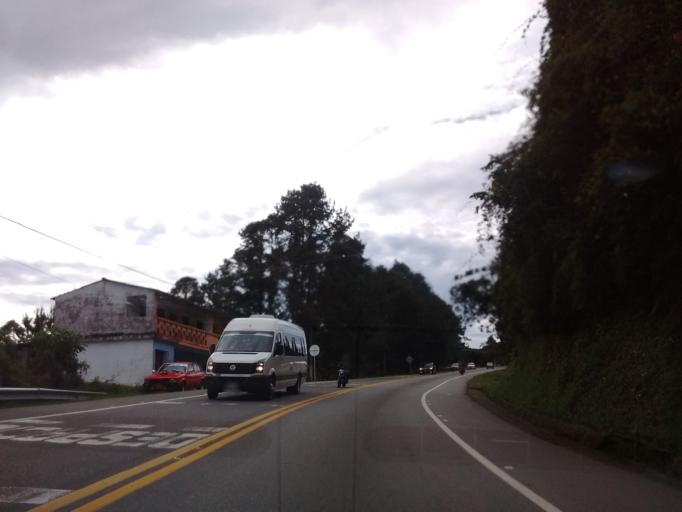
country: CO
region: Antioquia
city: Santuario
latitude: 6.1098
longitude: -75.2294
